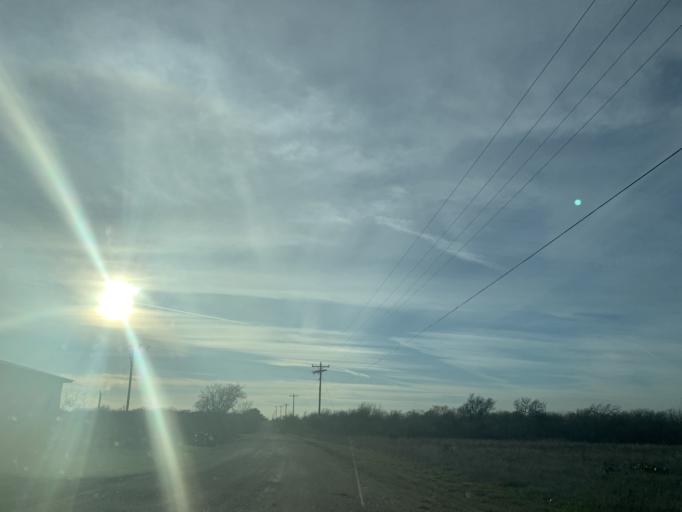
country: US
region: Texas
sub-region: Bell County
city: Salado
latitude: 30.8764
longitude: -97.5816
